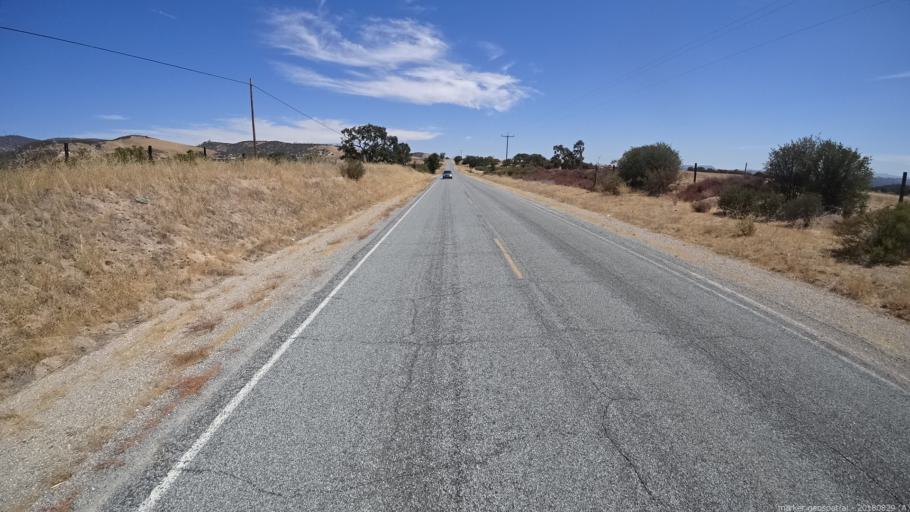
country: US
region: California
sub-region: San Luis Obispo County
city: Lake Nacimiento
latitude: 35.9306
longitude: -121.0526
